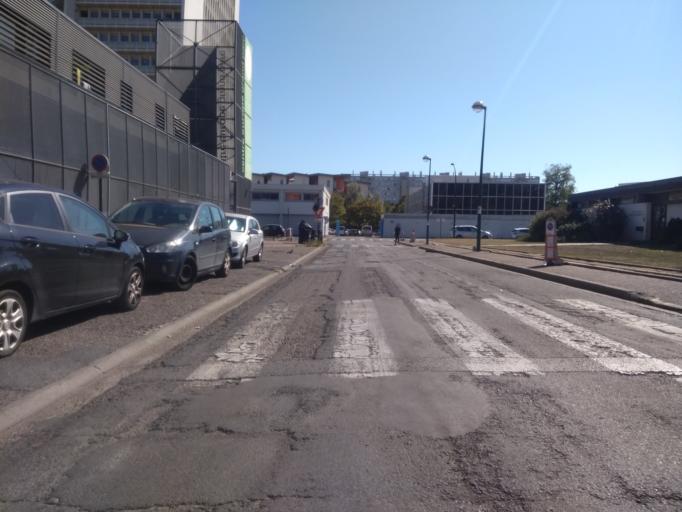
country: FR
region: Aquitaine
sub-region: Departement de la Gironde
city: Le Bouscat
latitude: 44.8593
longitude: -0.5835
